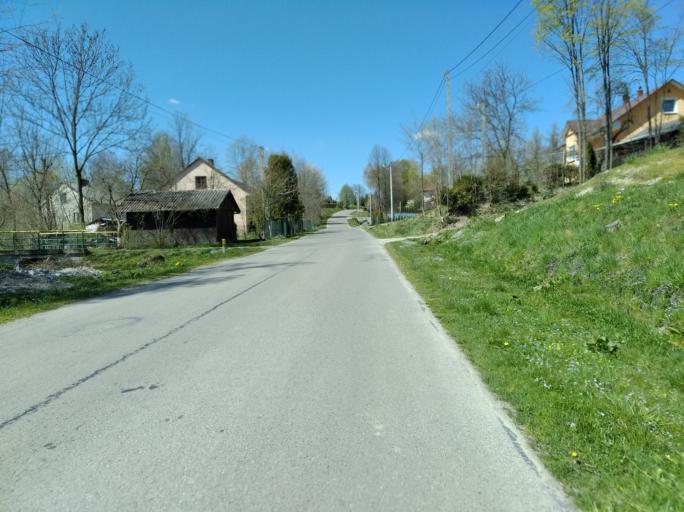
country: PL
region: Subcarpathian Voivodeship
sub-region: Powiat brzozowski
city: Jablonka
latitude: 49.7224
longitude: 22.1182
